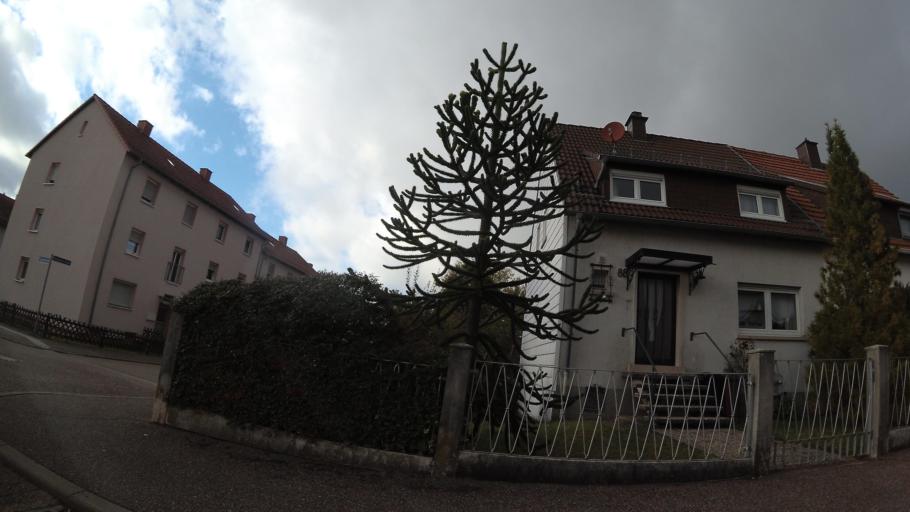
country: DE
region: Rheinland-Pfalz
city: Pirmasens
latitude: 49.1906
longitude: 7.5938
